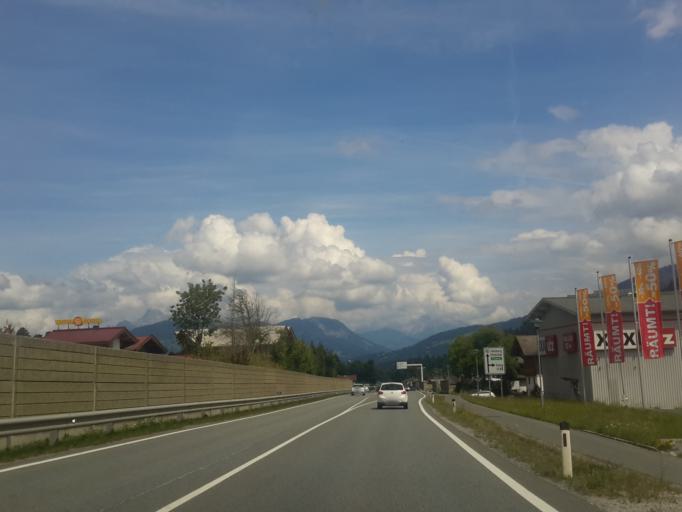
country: AT
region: Tyrol
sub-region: Politischer Bezirk Kufstein
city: Ellmau
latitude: 47.5156
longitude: 12.3213
